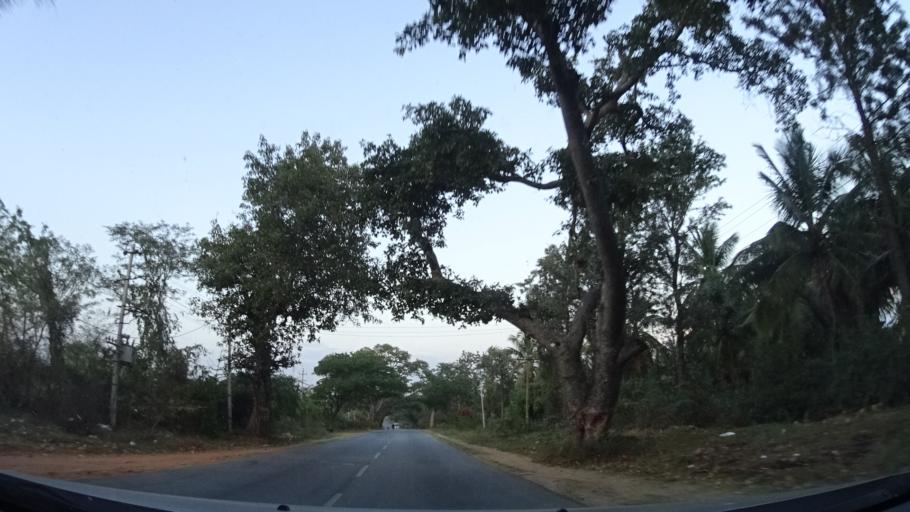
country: IN
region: Karnataka
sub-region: Ramanagara
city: Kanakapura
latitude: 12.6549
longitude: 77.4421
